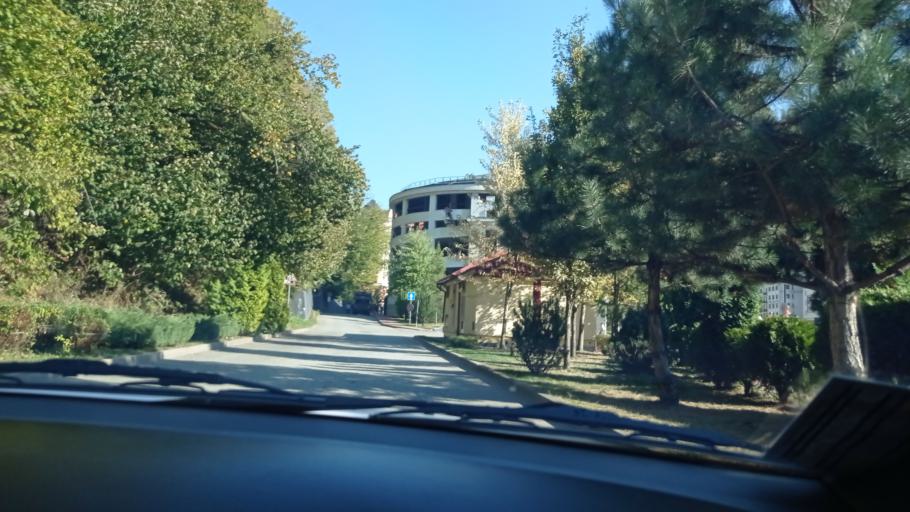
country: RU
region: Krasnodarskiy
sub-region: Sochi City
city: Krasnaya Polyana
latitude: 43.6735
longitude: 40.2916
